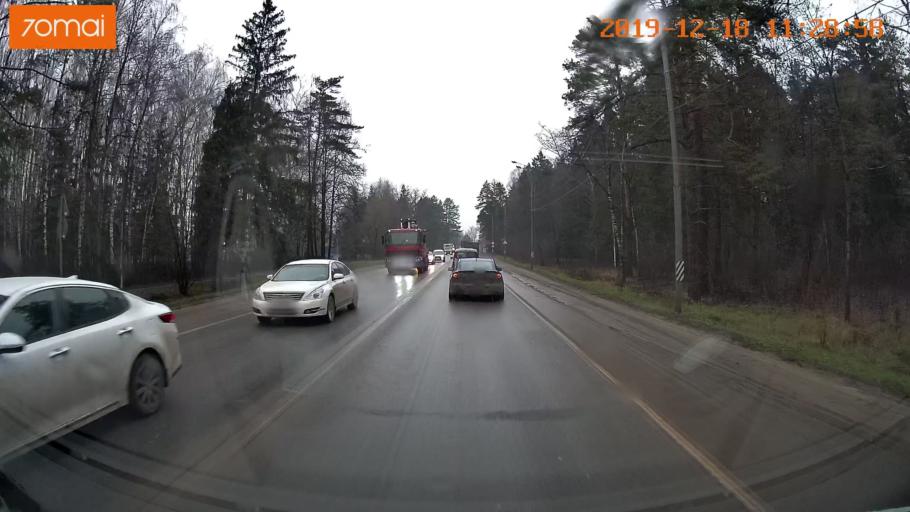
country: RU
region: Moskovskaya
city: Bol'shiye Vyazemy
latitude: 55.6461
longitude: 36.9753
